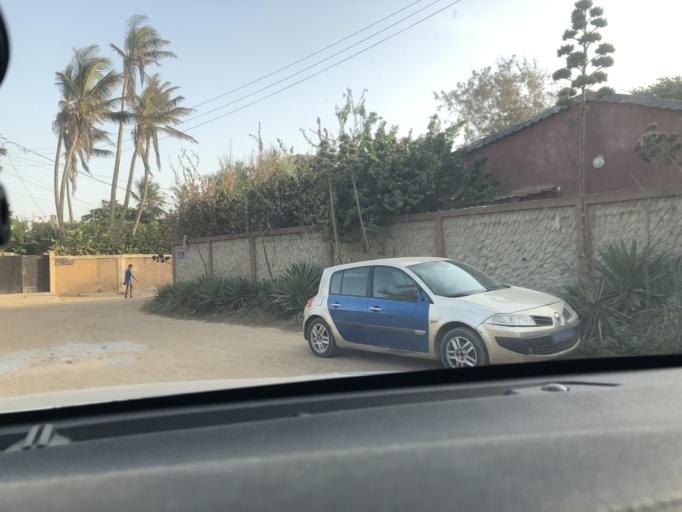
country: SN
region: Dakar
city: Mermoz Boabab
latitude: 14.7600
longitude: -17.4870
